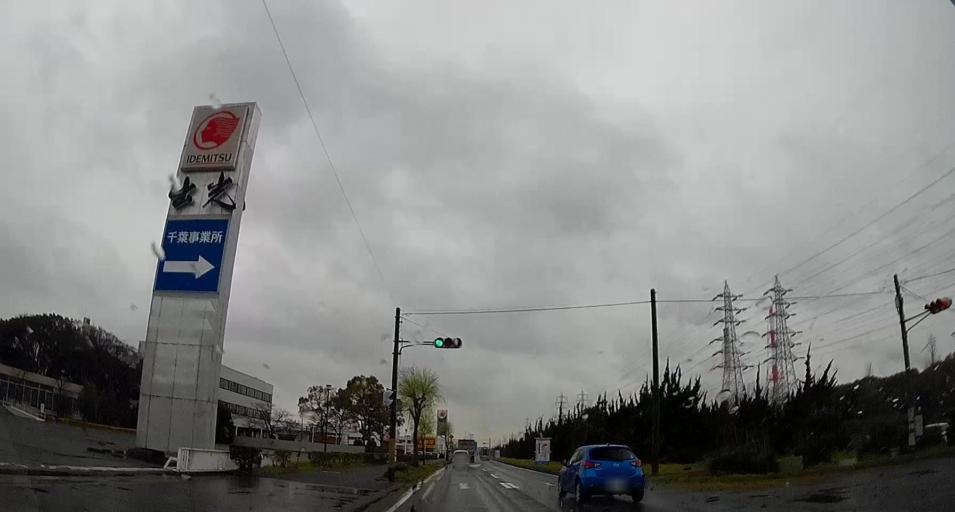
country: JP
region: Chiba
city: Ichihara
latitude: 35.4886
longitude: 140.0421
